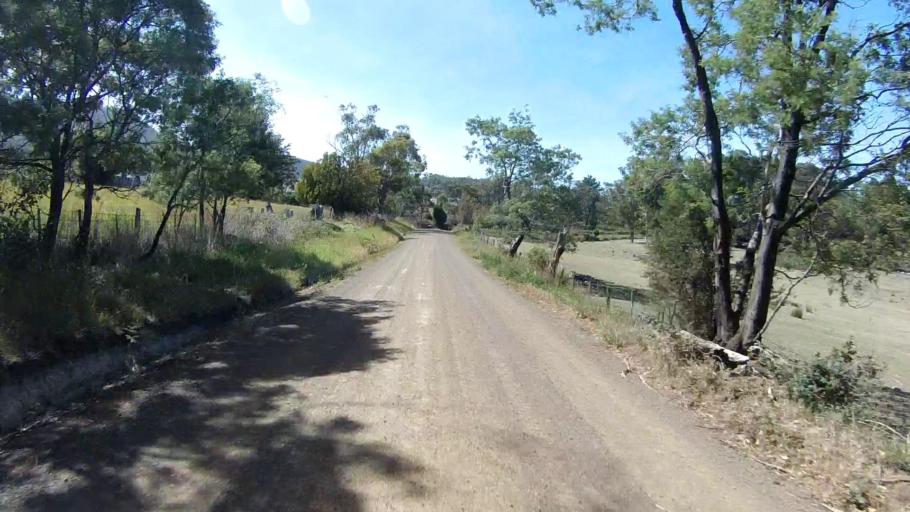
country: AU
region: Tasmania
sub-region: Sorell
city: Sorell
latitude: -42.7240
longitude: 147.5960
